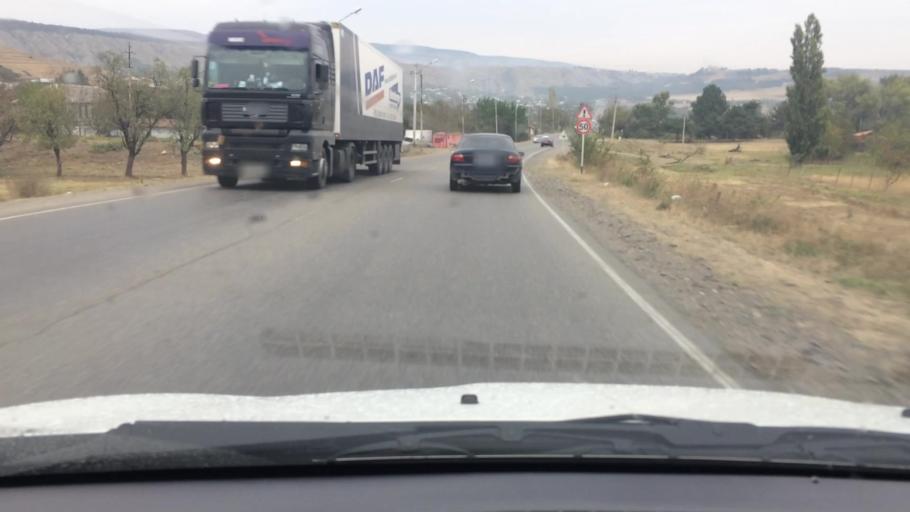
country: GE
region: T'bilisi
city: Tbilisi
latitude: 41.6025
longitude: 44.7792
